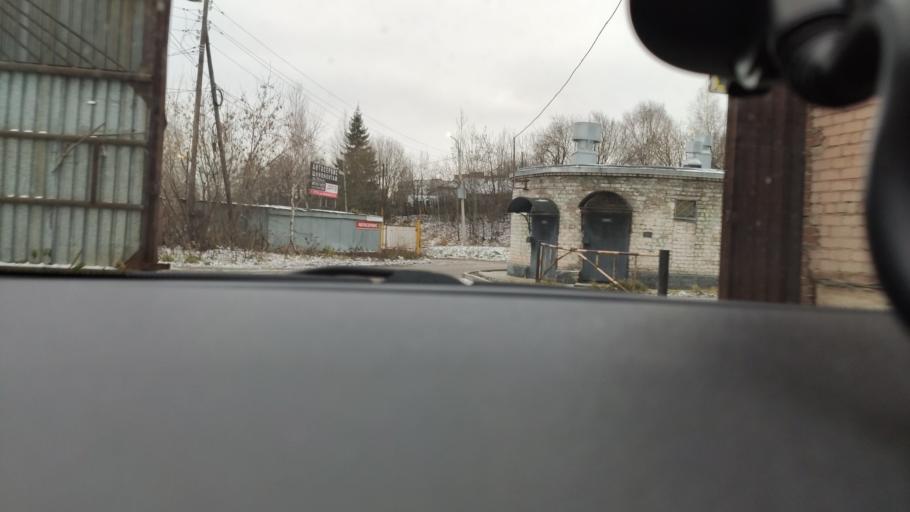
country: RU
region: Perm
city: Perm
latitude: 57.9841
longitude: 56.2762
